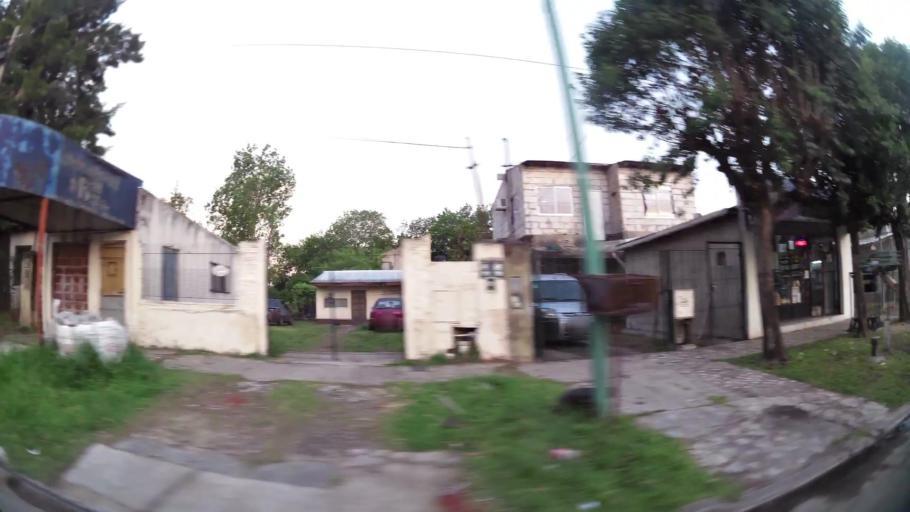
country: AR
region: Buenos Aires
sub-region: Partido de Lomas de Zamora
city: Lomas de Zamora
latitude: -34.7583
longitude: -58.3687
